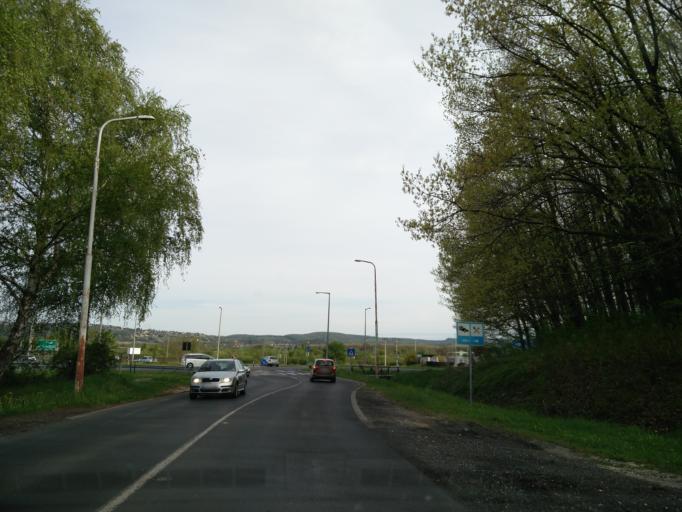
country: HU
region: Zala
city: Zalaegerszeg
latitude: 46.8608
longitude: 16.8499
